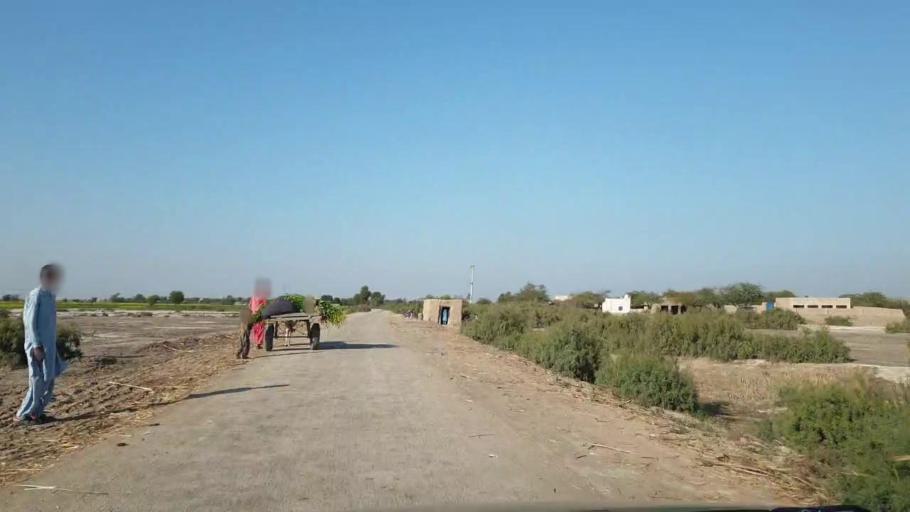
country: PK
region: Sindh
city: Khadro
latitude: 26.2063
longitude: 68.7543
